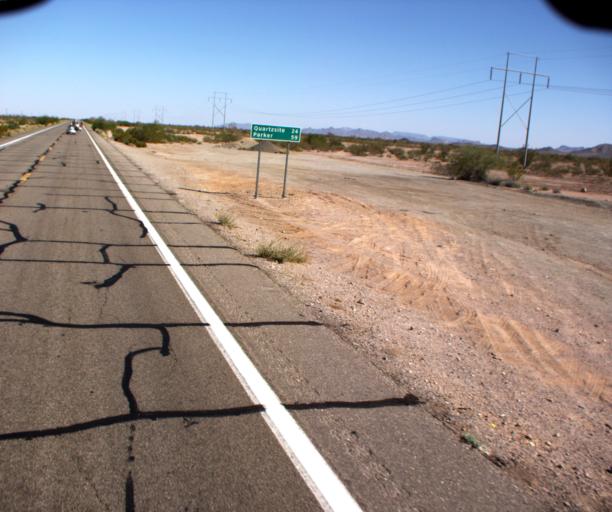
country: US
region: Arizona
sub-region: La Paz County
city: Quartzsite
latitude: 33.3117
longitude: -114.2169
